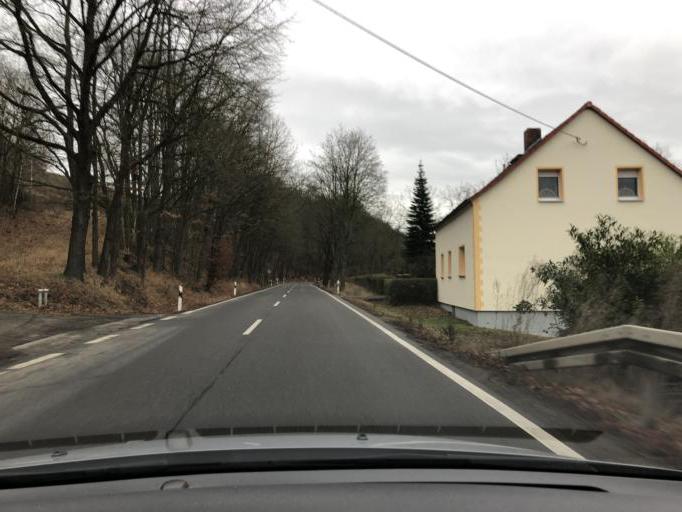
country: DE
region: Saxony
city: Niederstriegis
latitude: 51.0745
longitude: 13.1598
